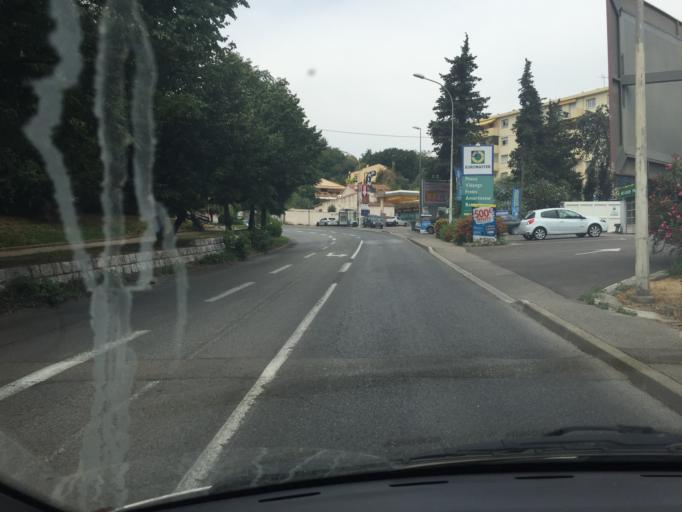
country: FR
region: Provence-Alpes-Cote d'Azur
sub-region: Departement des Alpes-Maritimes
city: Biot
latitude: 43.5939
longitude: 7.0988
